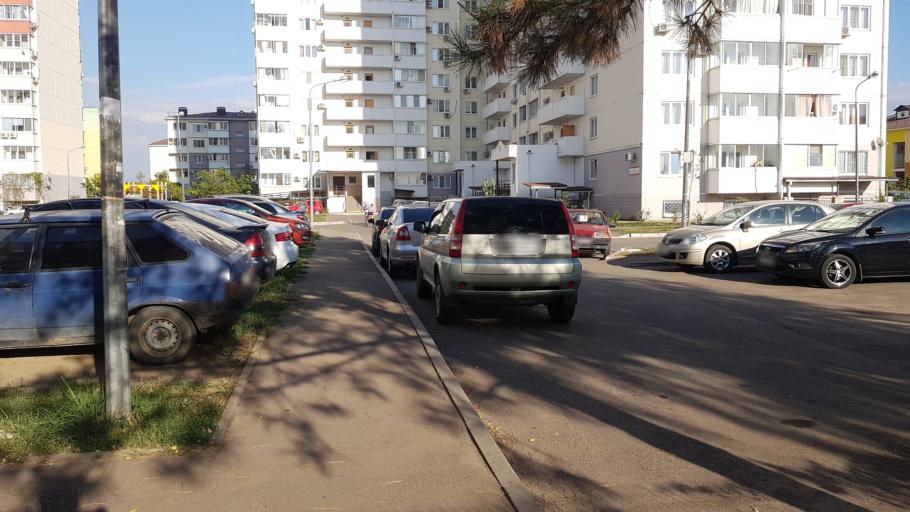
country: RU
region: Krasnodarskiy
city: Novotitarovskaya
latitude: 45.1444
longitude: 38.9930
